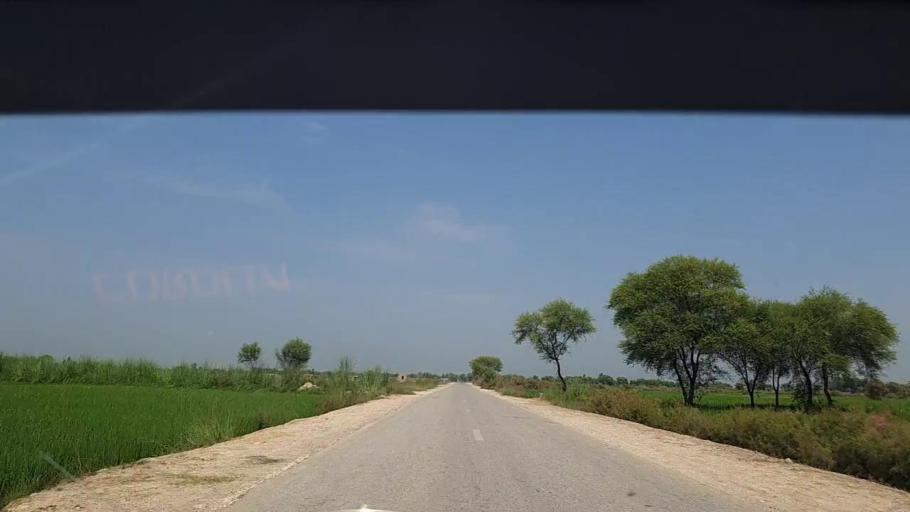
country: PK
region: Sindh
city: Thul
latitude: 28.1351
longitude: 68.8176
